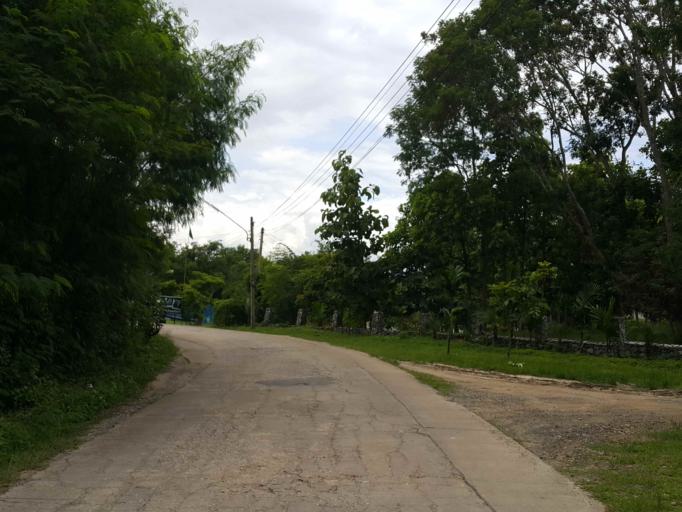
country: TH
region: Chiang Mai
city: San Sai
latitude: 18.9273
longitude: 98.9218
